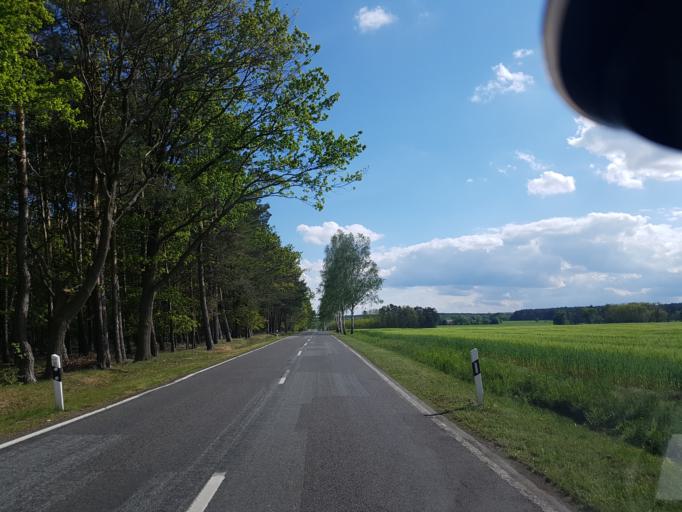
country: DE
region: Brandenburg
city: Drebkau
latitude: 51.6488
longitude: 14.2787
